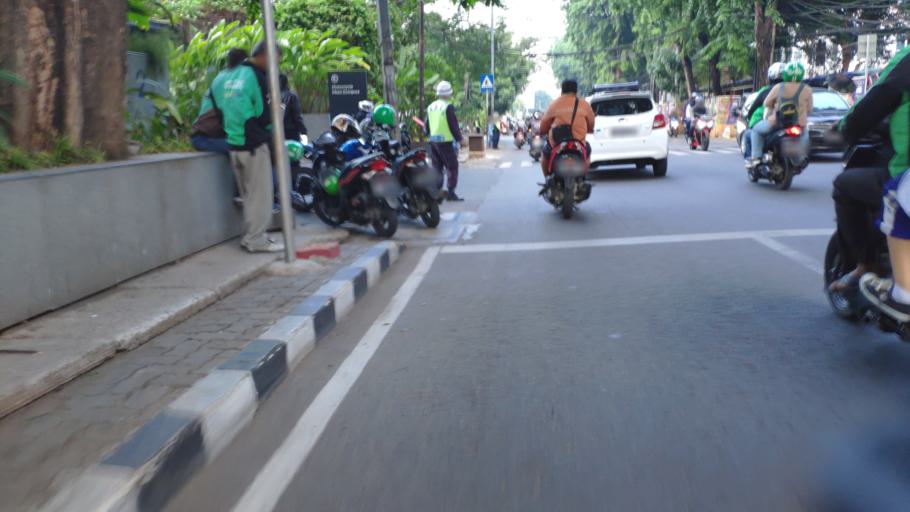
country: ID
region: Jakarta Raya
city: Jakarta
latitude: -6.2949
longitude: 106.8158
